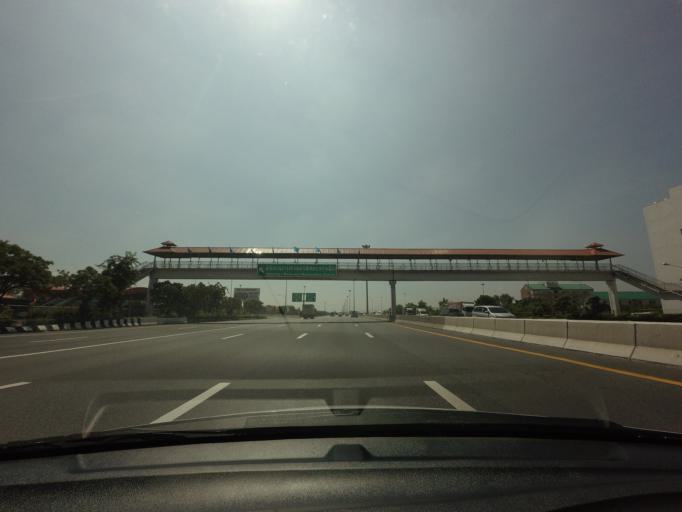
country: TH
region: Bangkok
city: Lat Krabang
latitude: 13.7060
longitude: 100.8222
